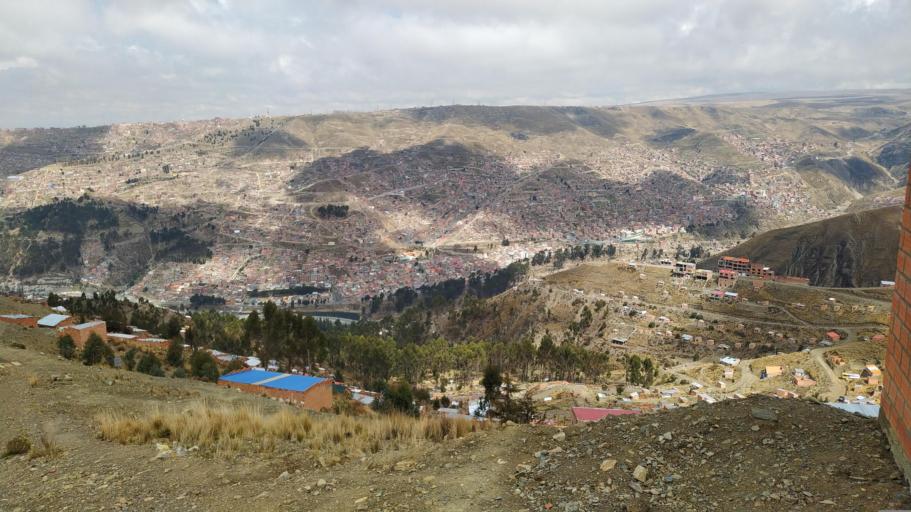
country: BO
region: La Paz
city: La Paz
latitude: -16.4653
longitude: -68.1384
